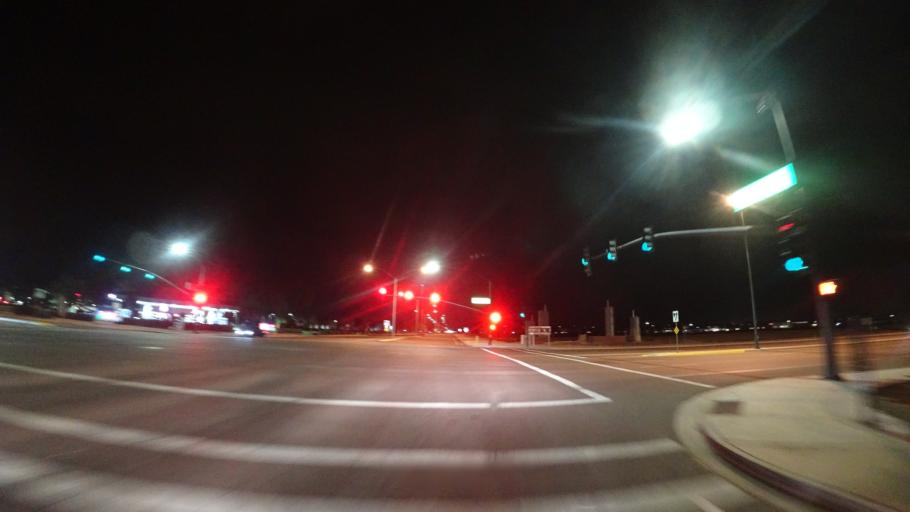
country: US
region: Arizona
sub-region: Maricopa County
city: Gilbert
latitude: 33.3792
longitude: -111.7226
